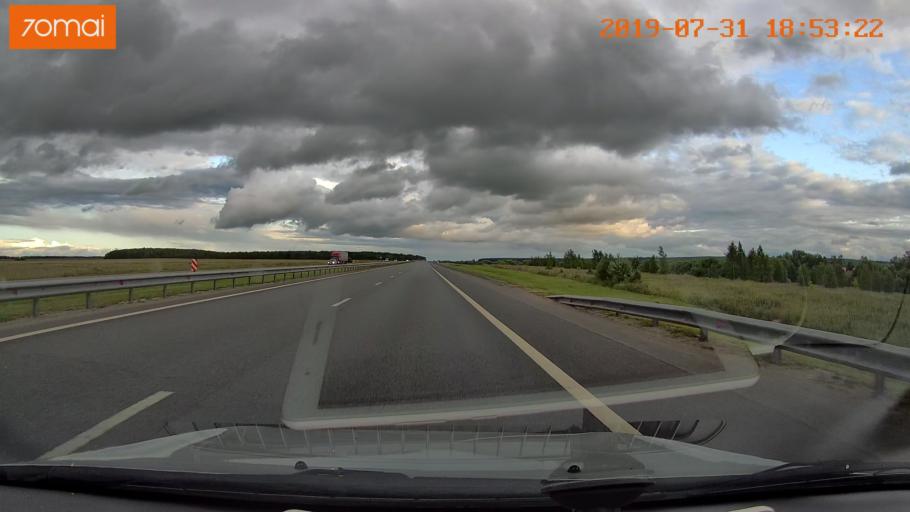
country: RU
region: Moskovskaya
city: Raduzhnyy
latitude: 55.2036
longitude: 38.6519
